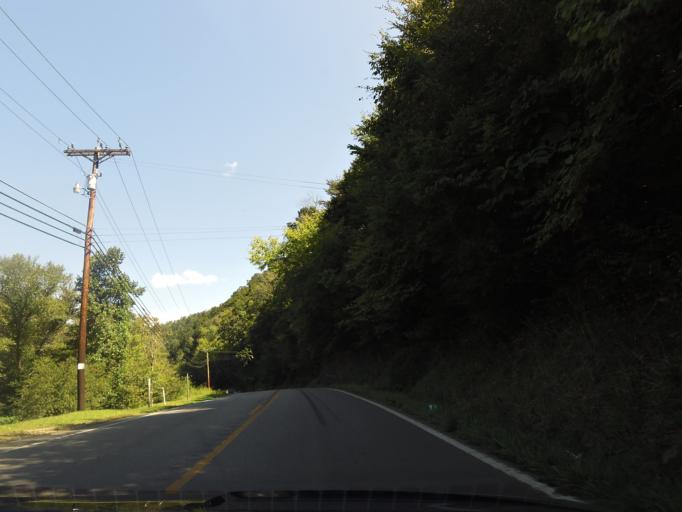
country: US
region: Kentucky
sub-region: Clay County
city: Manchester
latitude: 37.1602
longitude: -83.5851
